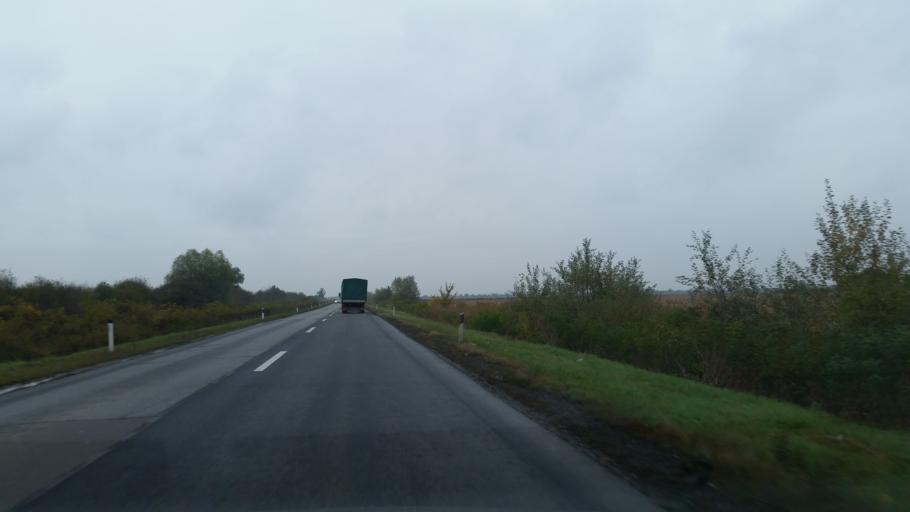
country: RS
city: Sefkerin
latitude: 44.9567
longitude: 20.4260
